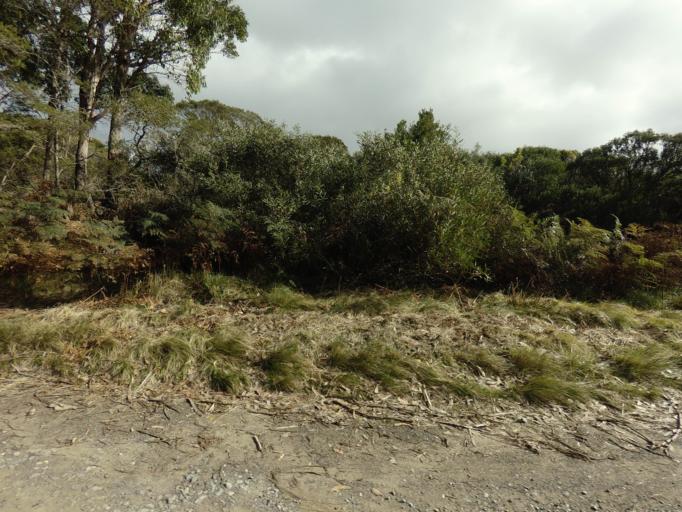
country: AU
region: Tasmania
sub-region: Huon Valley
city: Geeveston
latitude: -43.5793
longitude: 146.9004
